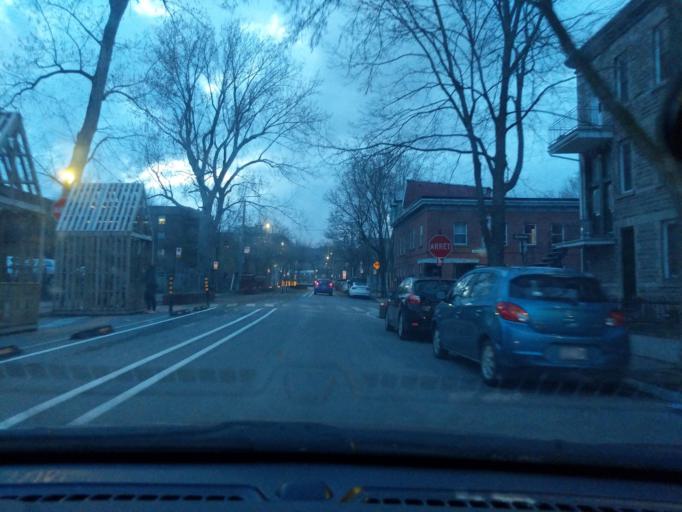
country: CA
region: Quebec
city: Westmount
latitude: 45.4818
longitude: -73.5649
